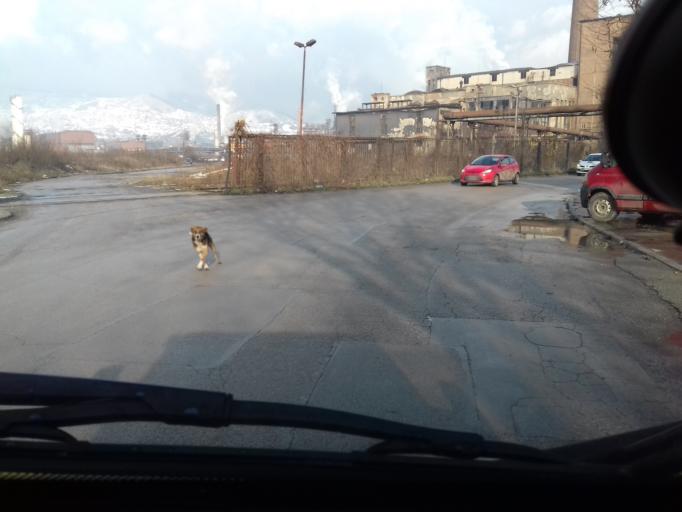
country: BA
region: Federation of Bosnia and Herzegovina
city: Zenica
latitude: 44.2110
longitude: 17.9041
